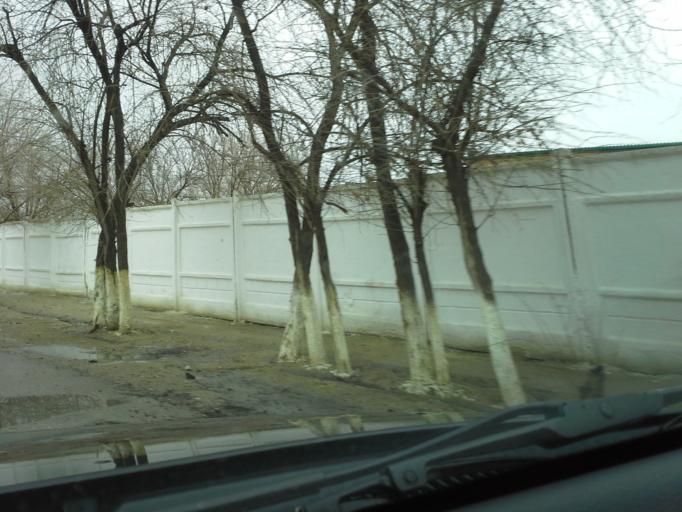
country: TM
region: Ahal
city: Ashgabat
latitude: 37.9501
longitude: 58.4233
